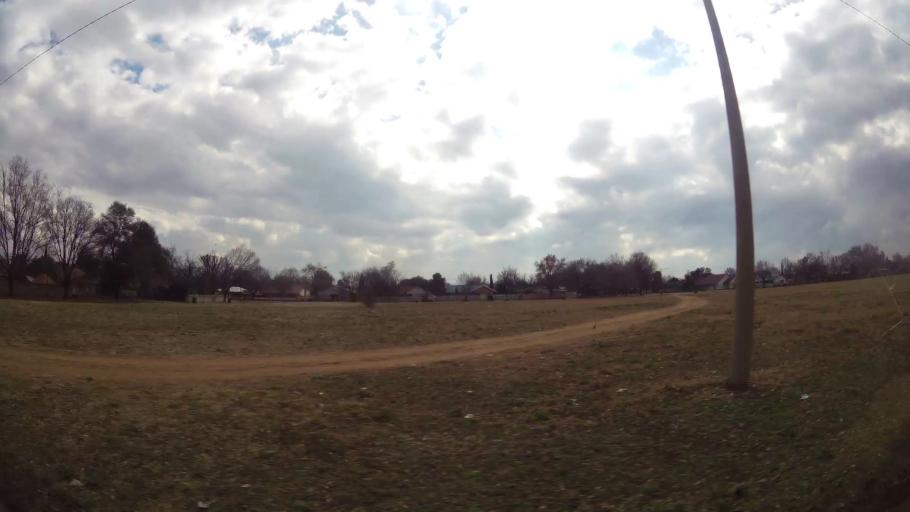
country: ZA
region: Gauteng
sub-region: Sedibeng District Municipality
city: Vereeniging
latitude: -26.6541
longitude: 27.9857
